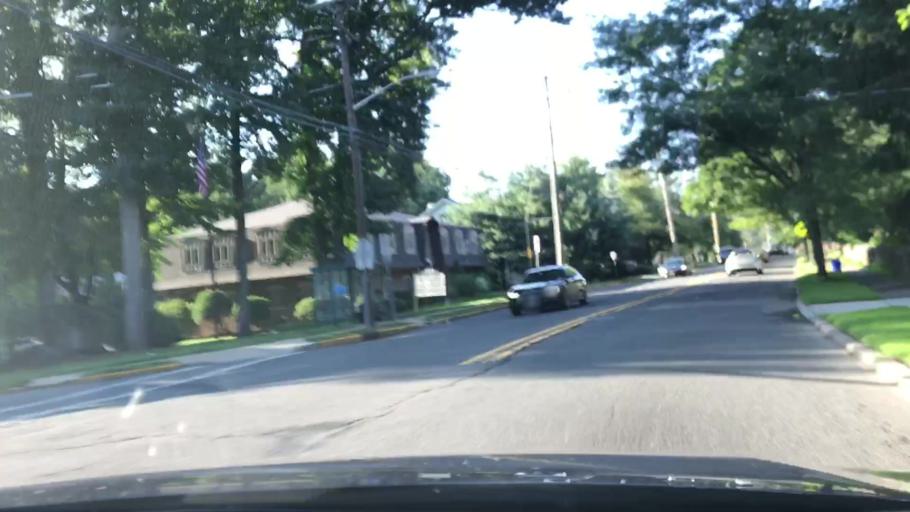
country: US
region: New Jersey
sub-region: Bergen County
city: Cresskill
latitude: 40.9385
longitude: -73.9573
